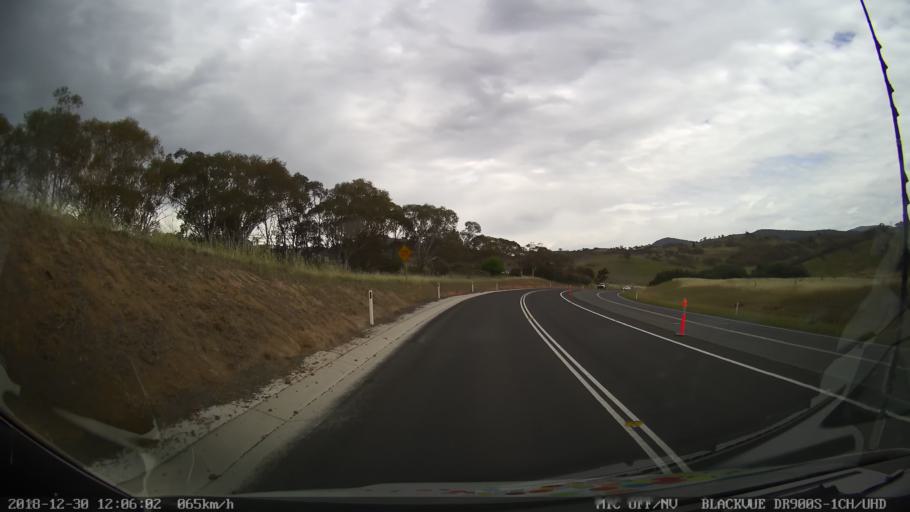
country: AU
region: New South Wales
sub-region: Snowy River
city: Jindabyne
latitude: -36.4135
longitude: 148.5986
